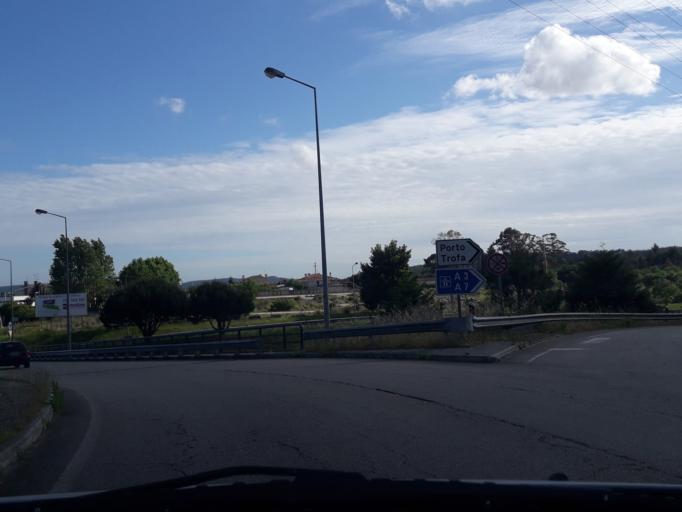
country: PT
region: Braga
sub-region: Vila Nova de Famalicao
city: Vila Nova de Famalicao
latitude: 41.3901
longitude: -8.5110
